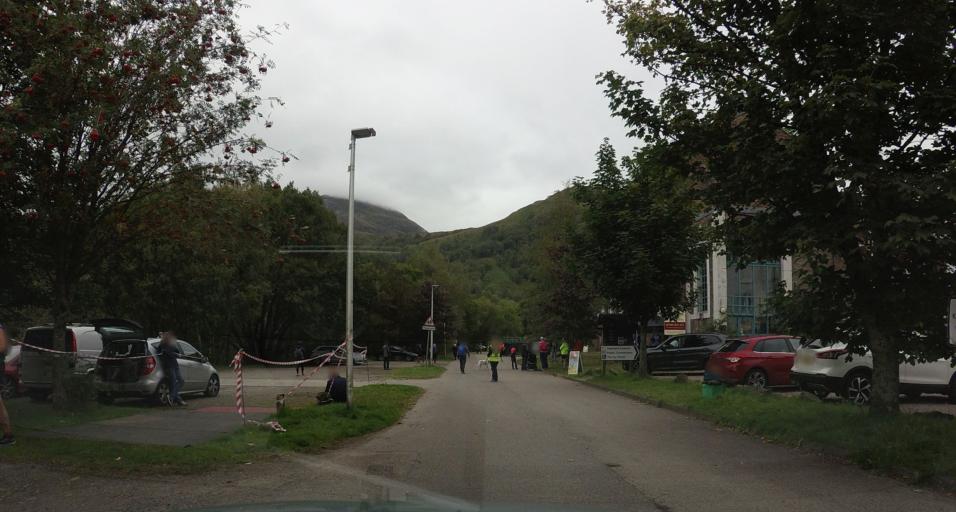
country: GB
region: Scotland
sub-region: Highland
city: Fort William
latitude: 56.7138
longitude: -4.9624
